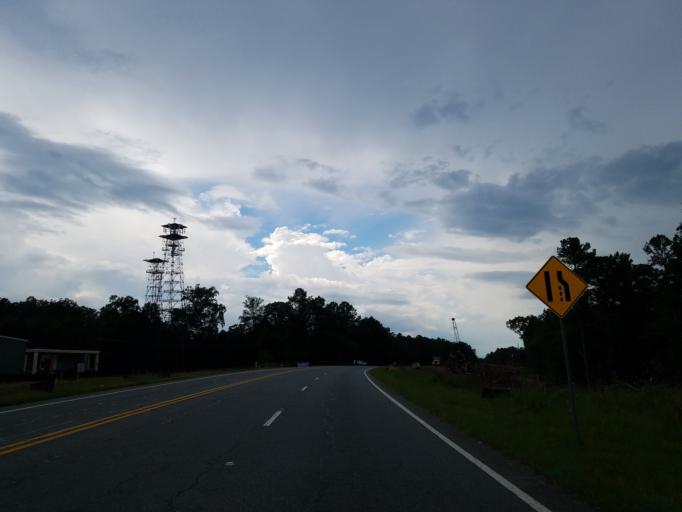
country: US
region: Georgia
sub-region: Bartow County
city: Adairsville
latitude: 34.3169
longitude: -84.8971
